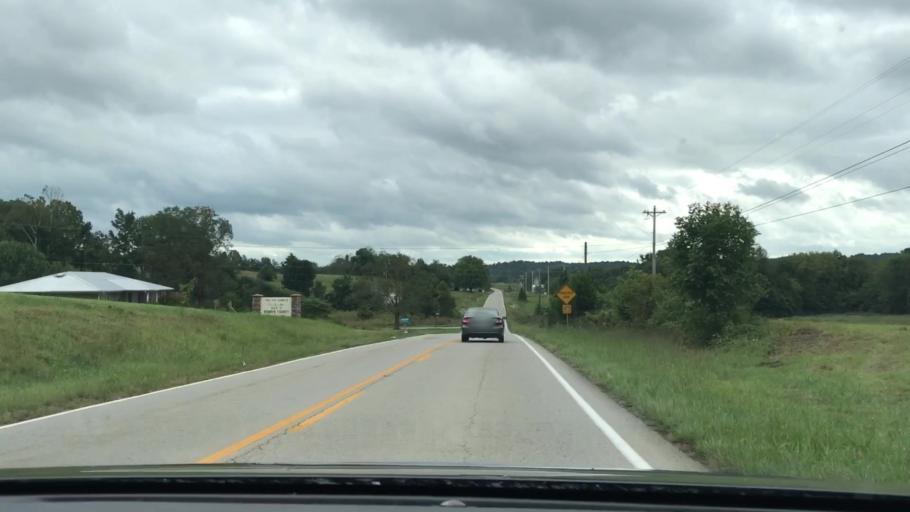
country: US
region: Kentucky
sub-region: Metcalfe County
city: Edmonton
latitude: 36.9043
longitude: -85.7533
